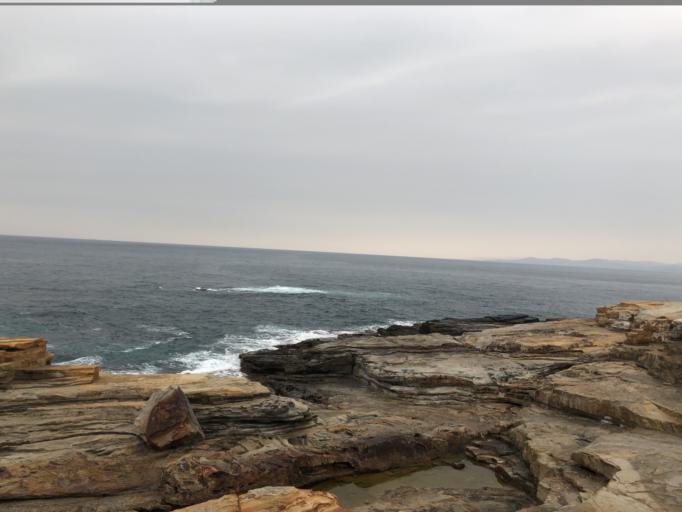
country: JP
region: Wakayama
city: Tanabe
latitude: 33.6707
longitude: 135.3306
